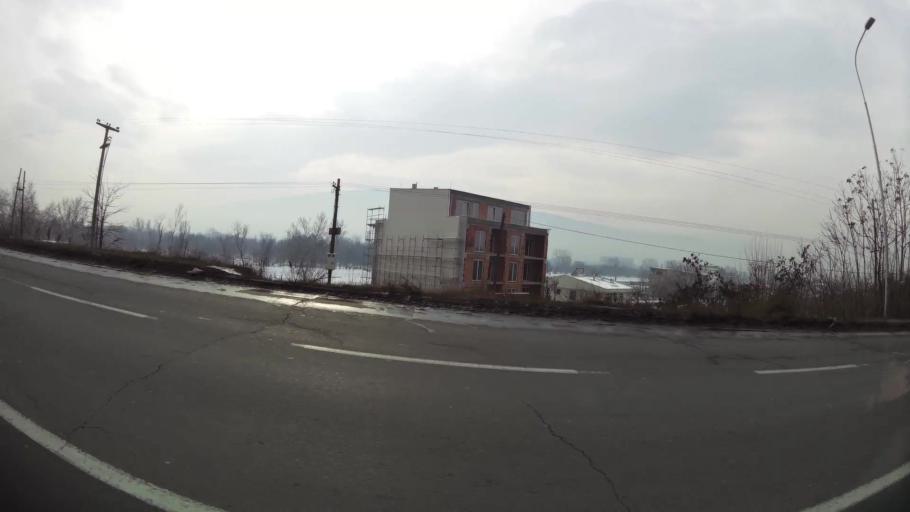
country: MK
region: Karpos
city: Skopje
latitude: 42.0144
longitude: 21.4145
